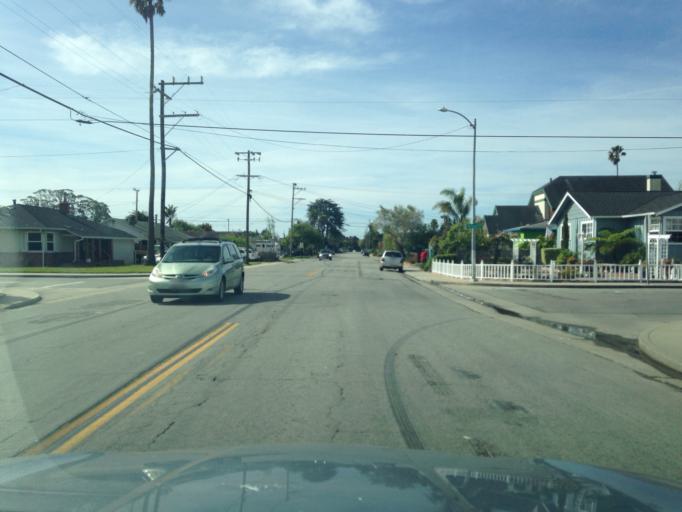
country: US
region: California
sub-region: Santa Cruz County
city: Santa Cruz
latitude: 36.9572
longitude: -122.0454
